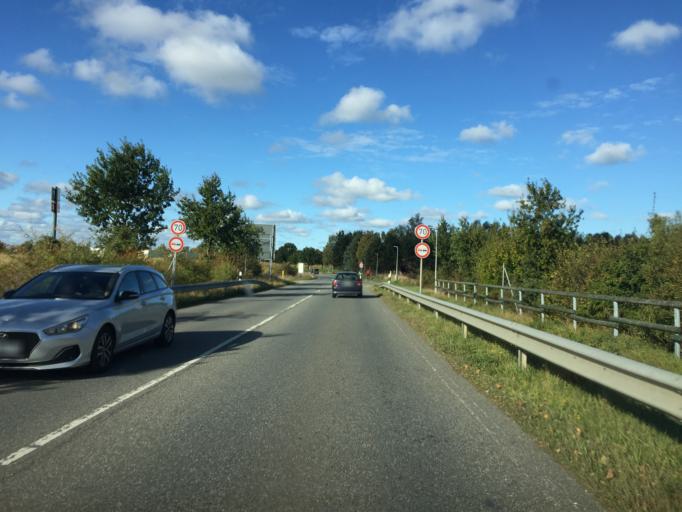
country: DE
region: Schleswig-Holstein
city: Oldenburg in Holstein
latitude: 54.2961
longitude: 10.8694
